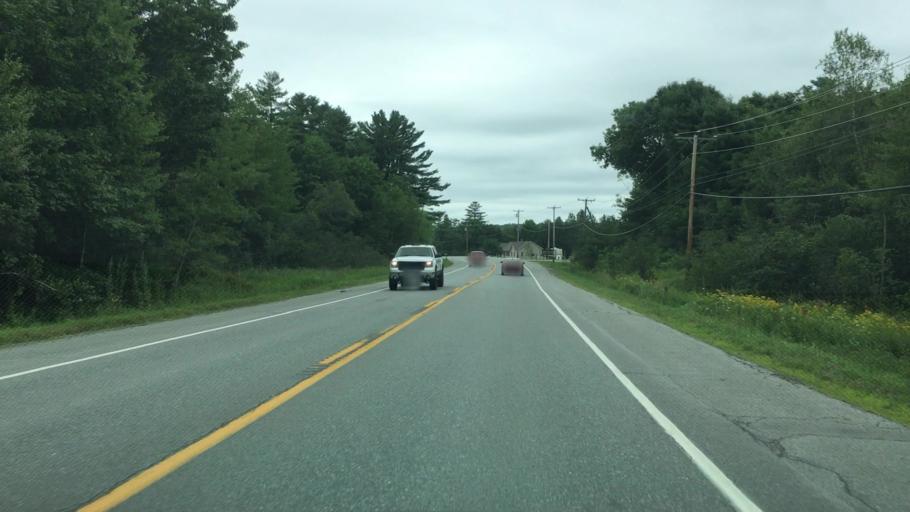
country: US
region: Maine
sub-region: Waldo County
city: Frankfort
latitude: 44.6173
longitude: -68.8698
